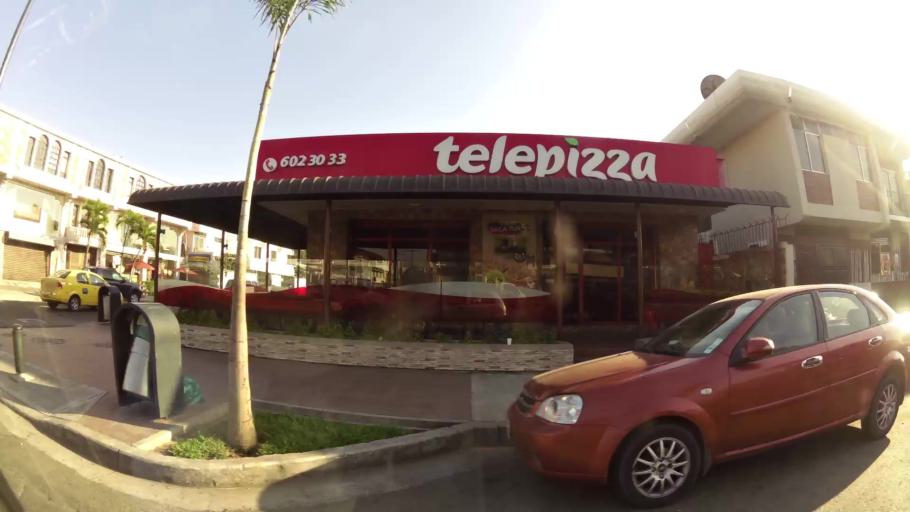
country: EC
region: Guayas
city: Guayaquil
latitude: -2.1633
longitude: -79.9135
